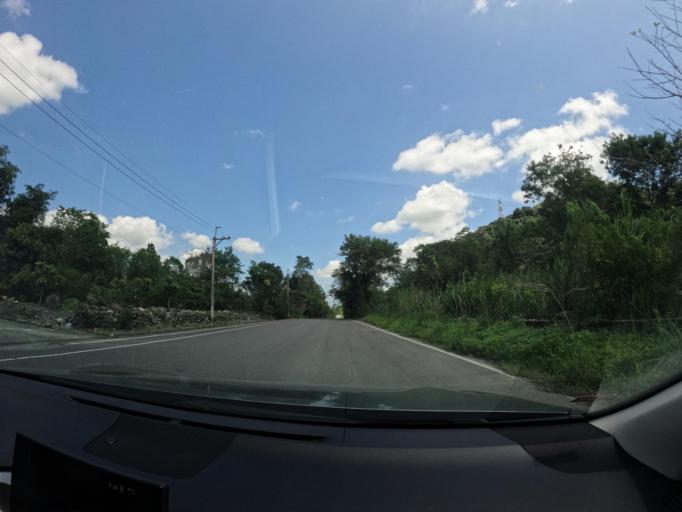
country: TW
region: Taiwan
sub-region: Hualien
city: Hualian
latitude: 23.6836
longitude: 121.3988
